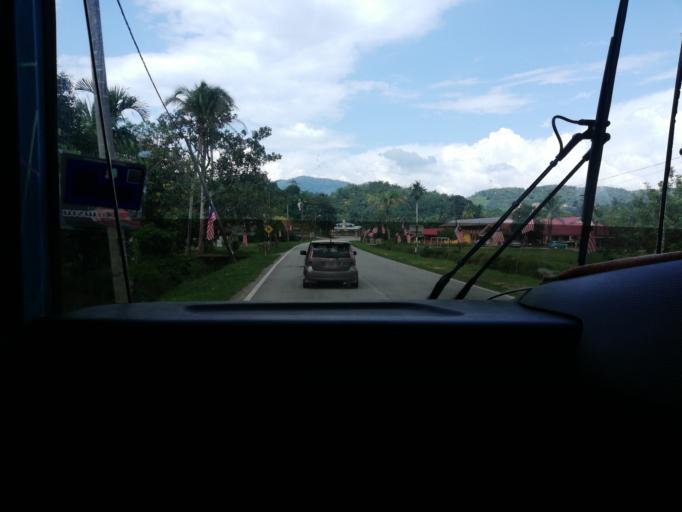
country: MY
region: Kedah
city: Kulim
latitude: 5.2842
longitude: 100.6252
